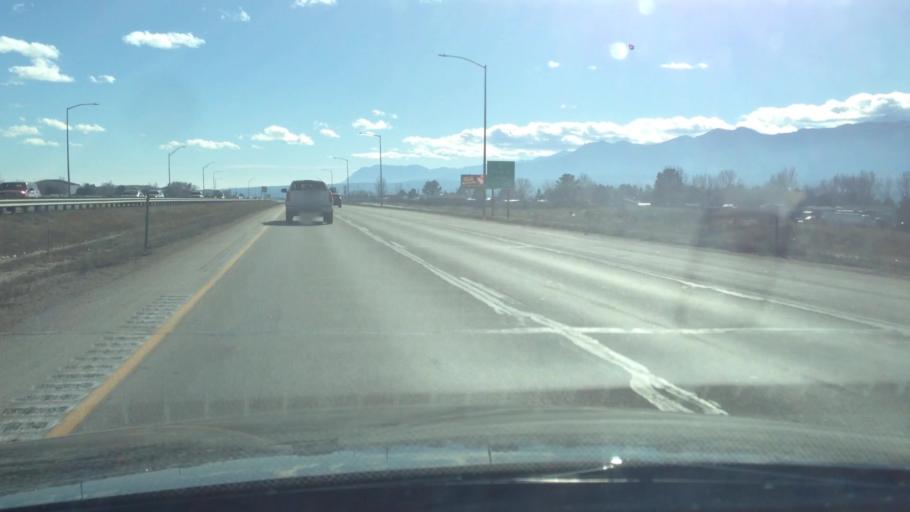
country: US
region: Colorado
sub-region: El Paso County
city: Monument
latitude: 39.1068
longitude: -104.8648
